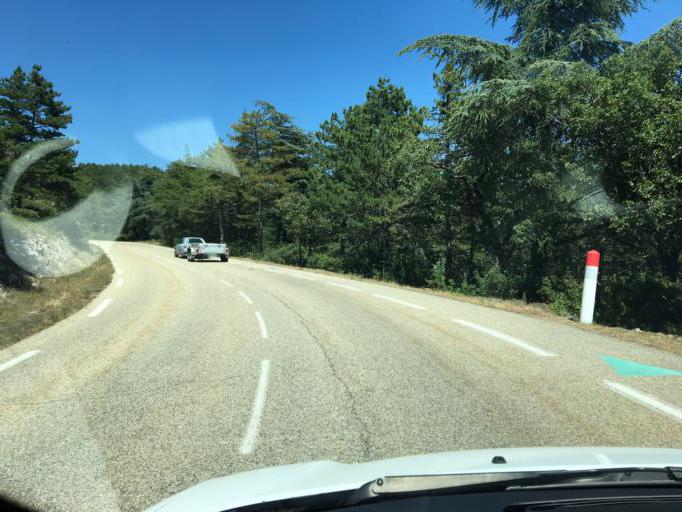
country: FR
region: Provence-Alpes-Cote d'Azur
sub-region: Departement du Vaucluse
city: Malaucene
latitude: 44.1625
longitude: 5.1587
